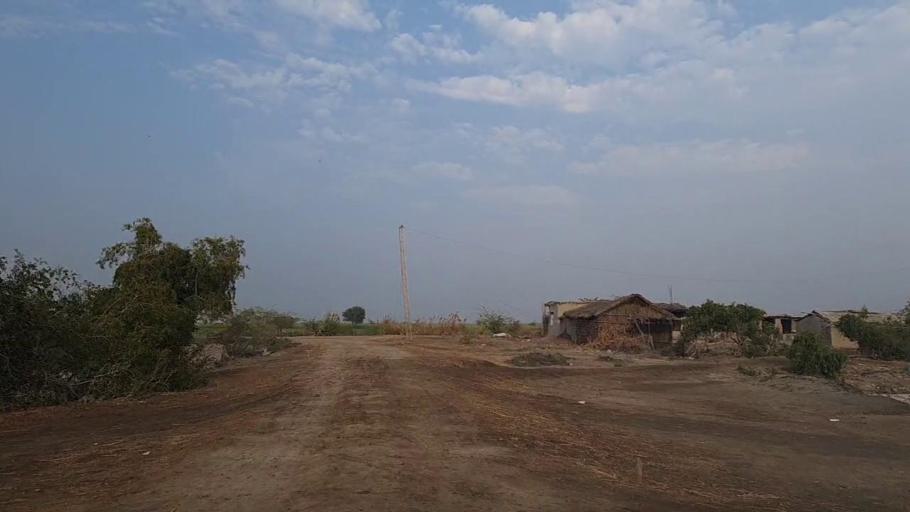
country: PK
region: Sindh
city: Mirwah Gorchani
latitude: 25.3188
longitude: 69.1973
